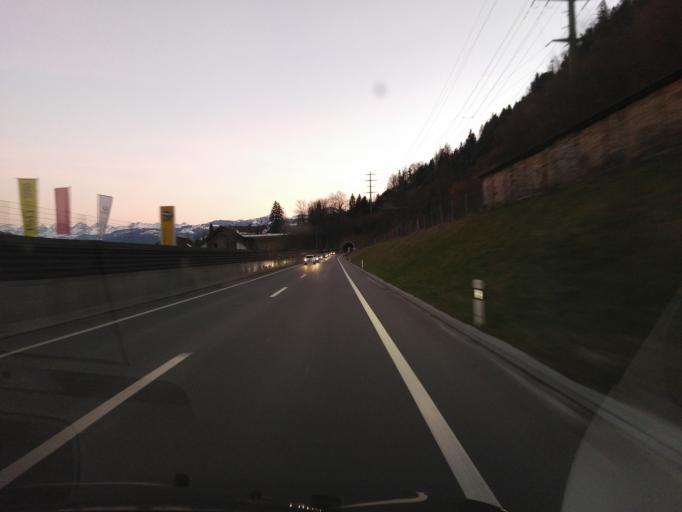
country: CH
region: Saint Gallen
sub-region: Wahlkreis Toggenburg
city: Wattwil
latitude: 47.3066
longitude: 9.0786
